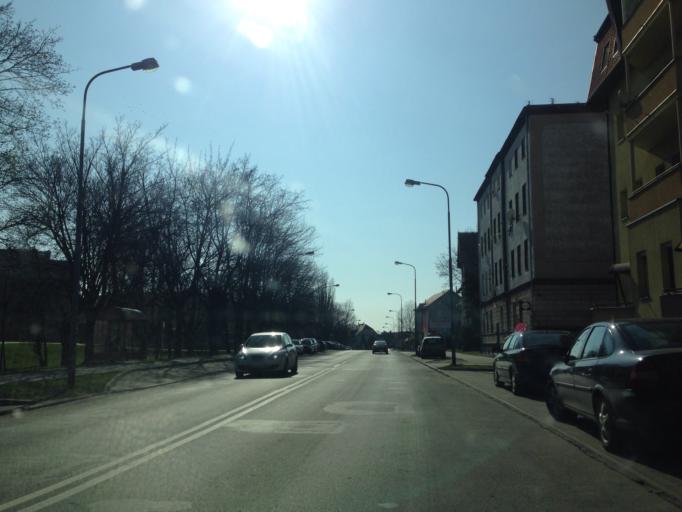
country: PL
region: Lower Silesian Voivodeship
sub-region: Powiat olesnicki
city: Olesnica
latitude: 51.2125
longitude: 17.3807
